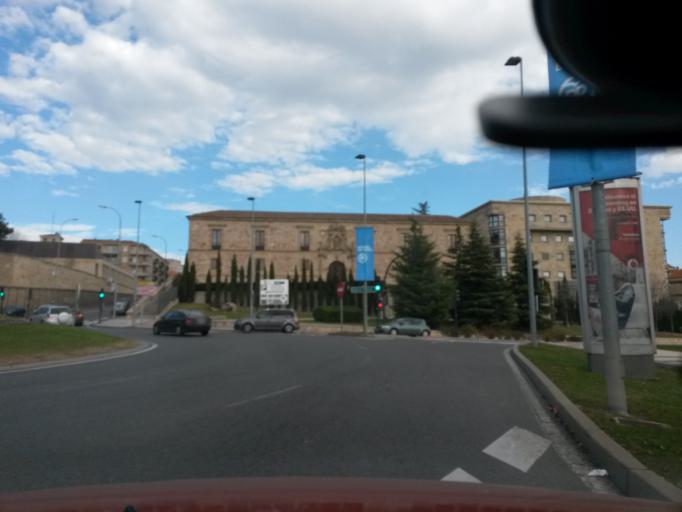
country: ES
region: Castille and Leon
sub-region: Provincia de Salamanca
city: Salamanca
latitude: 40.9578
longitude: -5.6607
